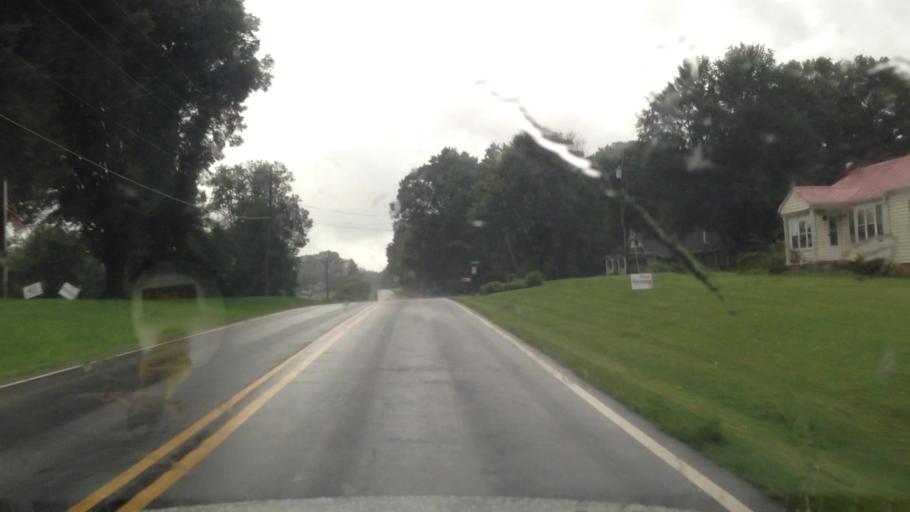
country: US
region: North Carolina
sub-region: Rockingham County
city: Reidsville
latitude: 36.2838
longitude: -79.7370
